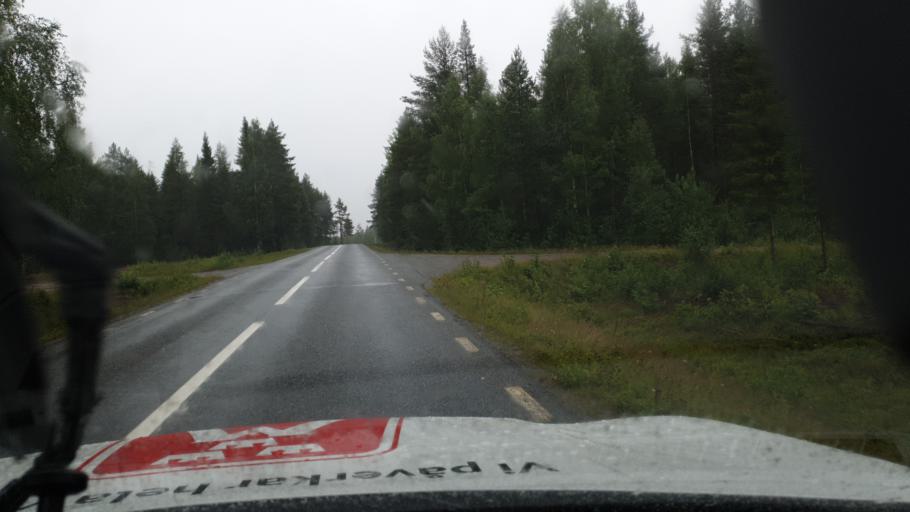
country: SE
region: Vaesterbotten
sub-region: Skelleftea Kommun
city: Burtraesk
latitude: 64.4046
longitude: 20.3857
